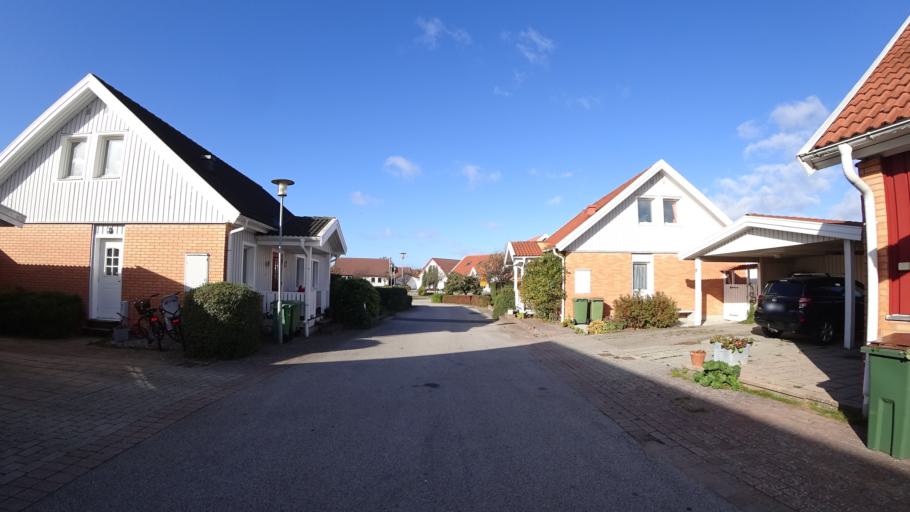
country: SE
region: Skane
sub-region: Staffanstorps Kommun
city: Hjaerup
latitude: 55.6755
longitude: 13.1435
